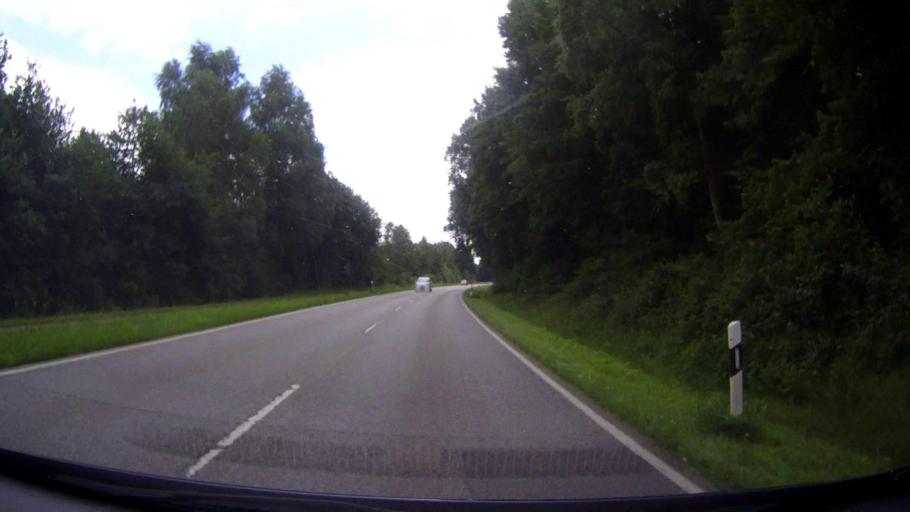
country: DE
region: Schleswig-Holstein
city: Meezen
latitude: 54.0730
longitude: 9.7290
